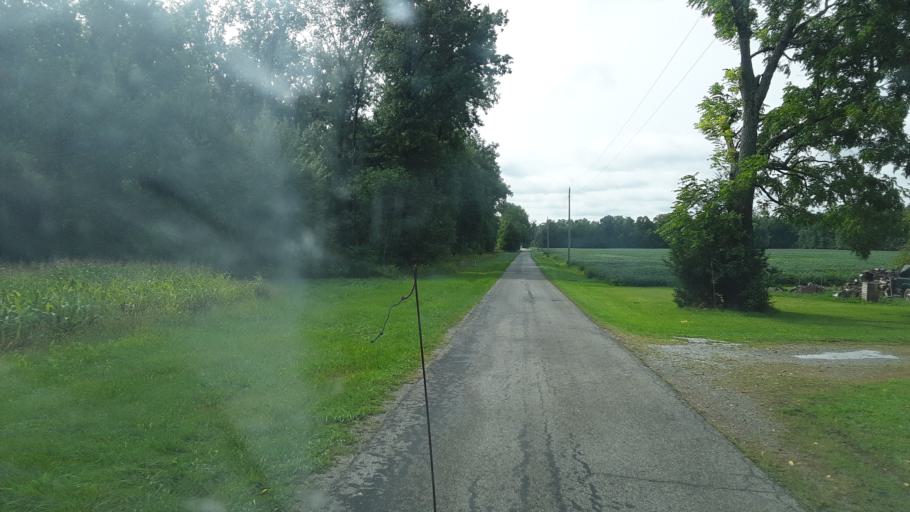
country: US
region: Ohio
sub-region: Morrow County
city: Cardington
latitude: 40.5274
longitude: -82.9768
